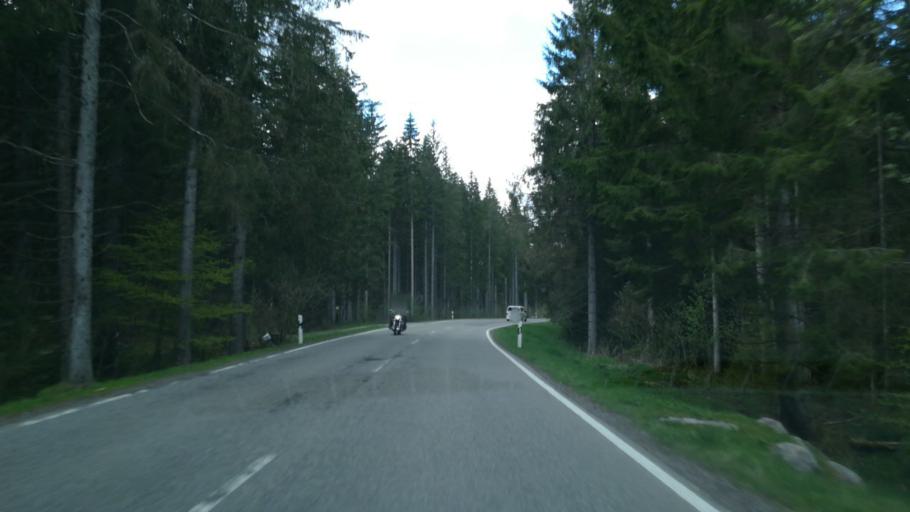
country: DE
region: Baden-Wuerttemberg
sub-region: Freiburg Region
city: Schluchsee
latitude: 47.7997
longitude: 8.2032
